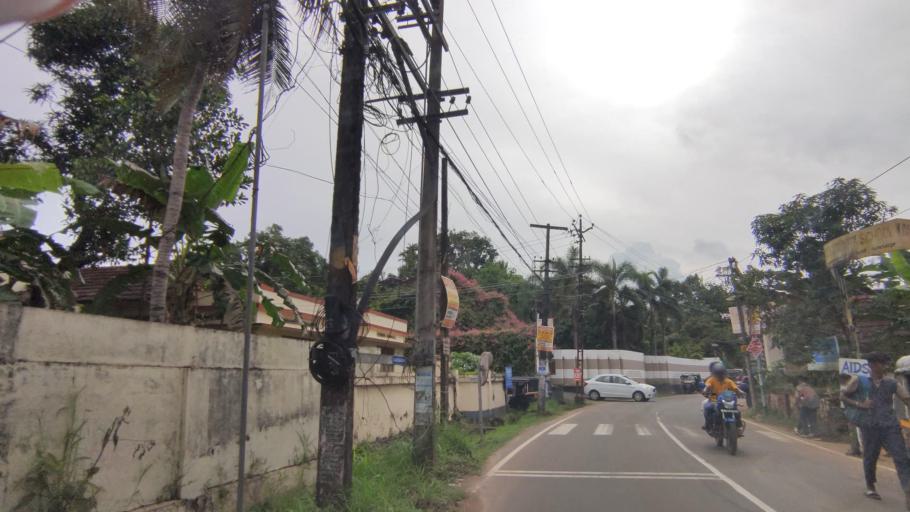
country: IN
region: Kerala
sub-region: Kottayam
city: Kottayam
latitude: 9.5830
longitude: 76.5119
